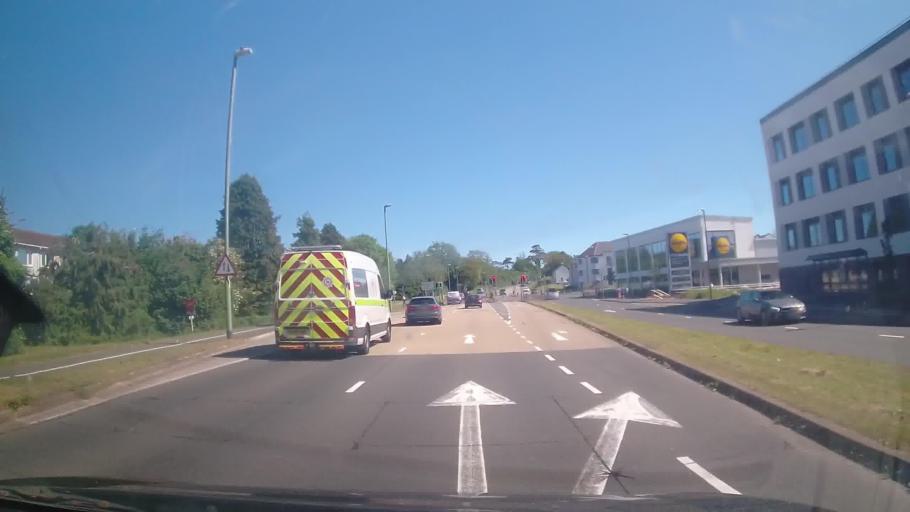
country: GB
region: England
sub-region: Borough of Torbay
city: Paignton
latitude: 50.4137
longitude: -3.5784
